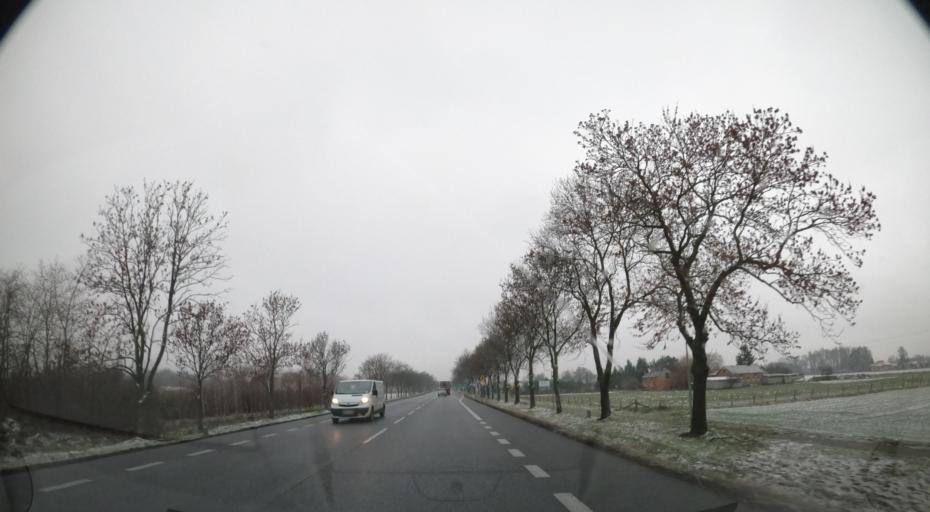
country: PL
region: Masovian Voivodeship
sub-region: Powiat sochaczewski
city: Sochaczew
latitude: 52.2223
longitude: 20.3171
